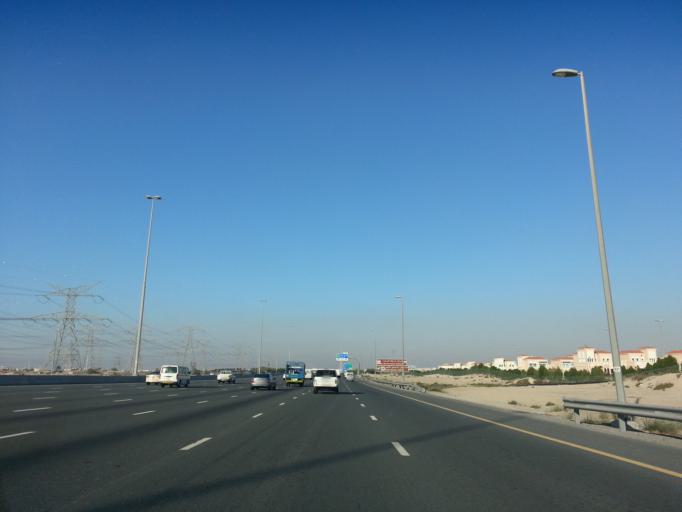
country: AE
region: Dubai
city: Dubai
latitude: 25.0702
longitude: 55.2050
